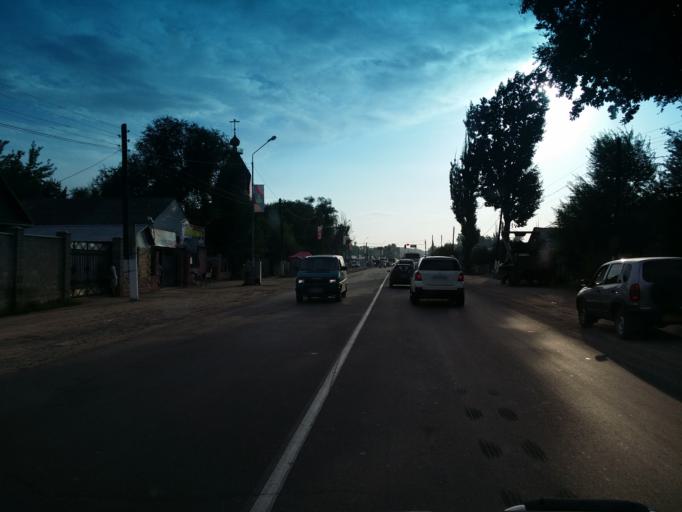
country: KZ
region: Almaty Oblysy
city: Talghar
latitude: 43.4049
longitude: 77.2239
